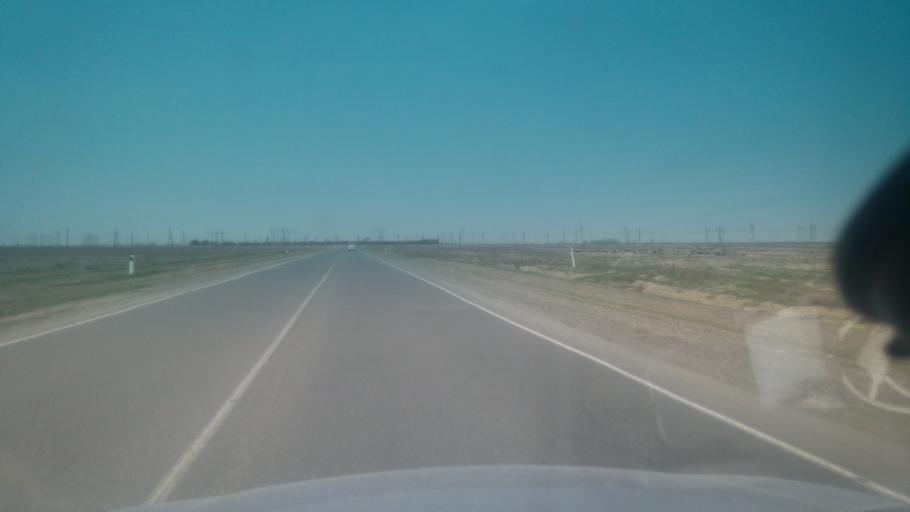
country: UZ
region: Jizzax
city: Dashtobod
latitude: 40.1528
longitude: 68.5467
